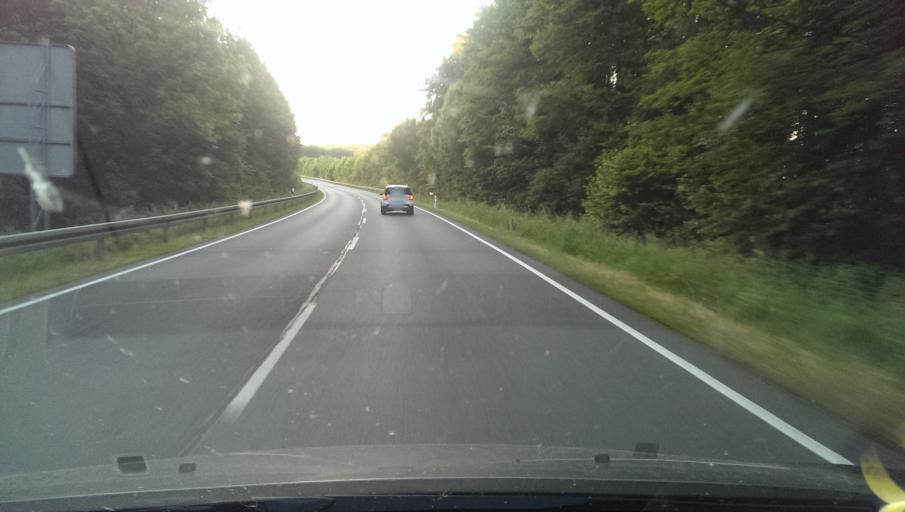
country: DE
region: Bavaria
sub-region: Regierungsbezirk Unterfranken
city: Wuerzburg
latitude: 49.7676
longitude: 9.8584
